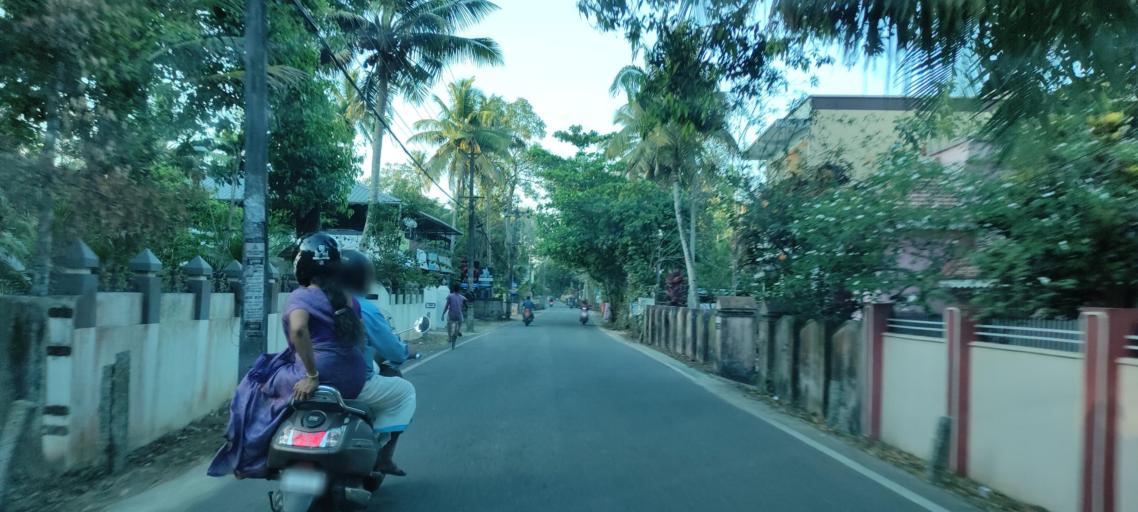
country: IN
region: Kerala
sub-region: Alappuzha
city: Kayankulam
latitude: 9.2213
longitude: 76.4604
